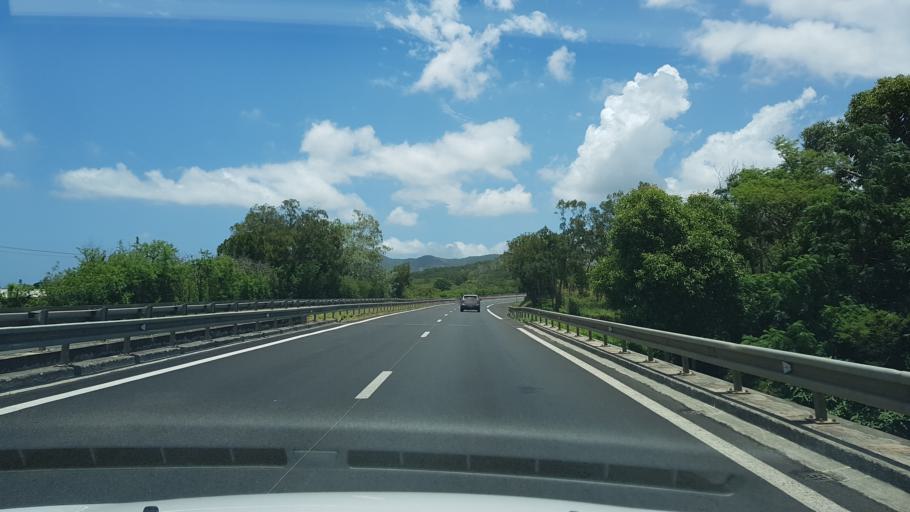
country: NC
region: South Province
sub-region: Paita
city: Paita
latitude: -22.1566
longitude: 166.3769
